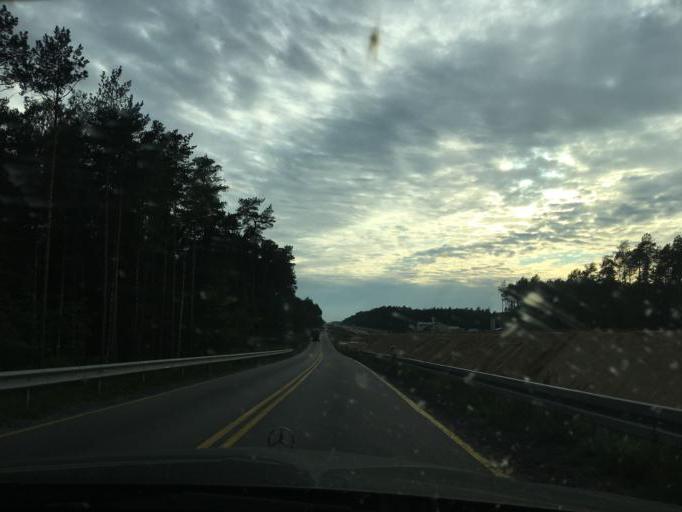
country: PL
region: Masovian Voivodeship
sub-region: Powiat ostrowski
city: Ostrow Mazowiecka
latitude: 52.7775
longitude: 21.8439
